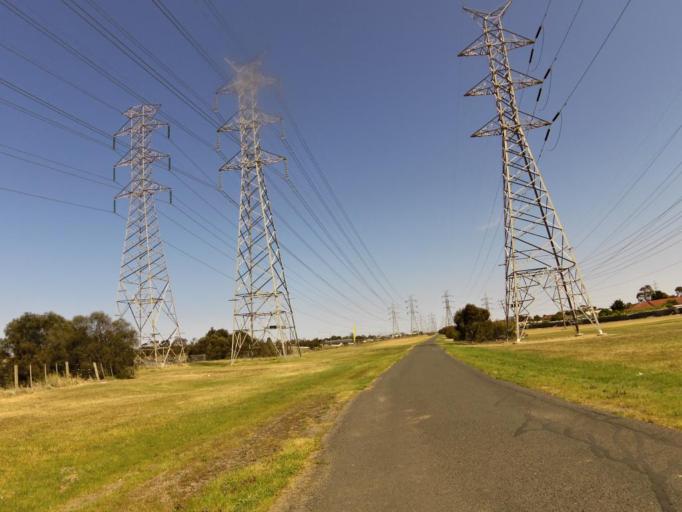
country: AU
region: Victoria
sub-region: Brimbank
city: Kealba
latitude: -37.7504
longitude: 144.8309
